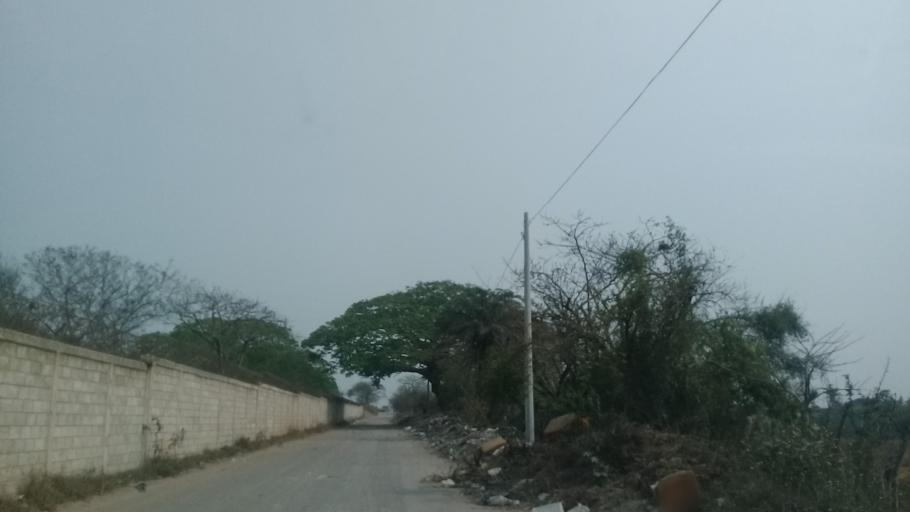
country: MX
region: Veracruz
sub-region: Veracruz
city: Lomas de Rio Medio Cuatro
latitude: 19.1890
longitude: -96.2224
